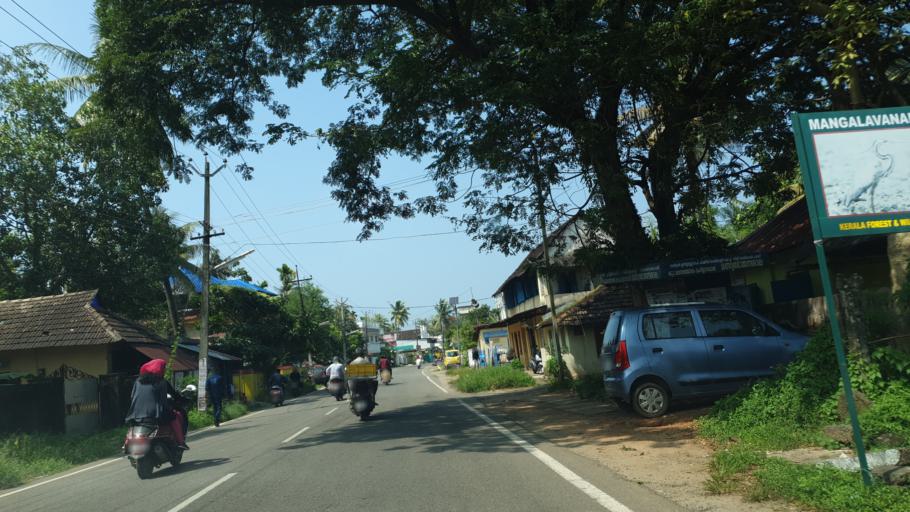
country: IN
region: Kerala
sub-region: Ernakulam
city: Cochin
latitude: 9.9756
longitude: 76.2422
